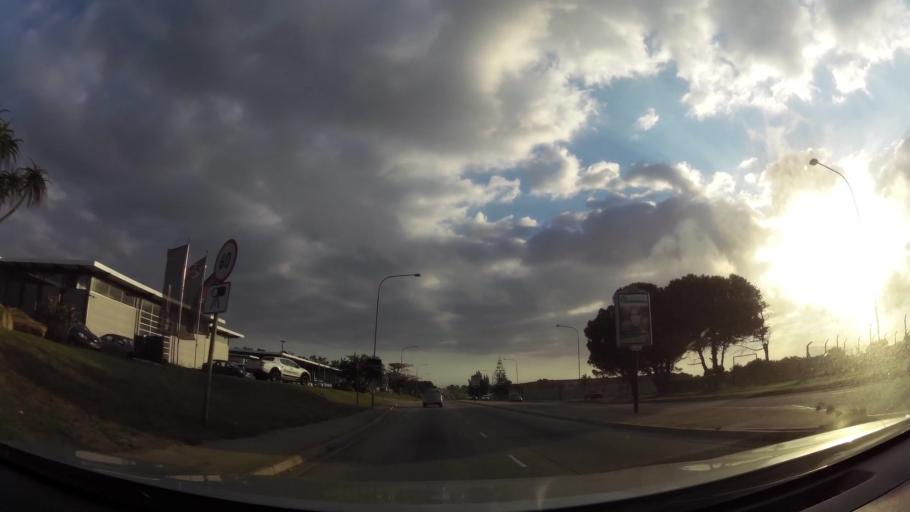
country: ZA
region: Eastern Cape
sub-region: Nelson Mandela Bay Metropolitan Municipality
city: Port Elizabeth
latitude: -33.9788
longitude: 25.5535
